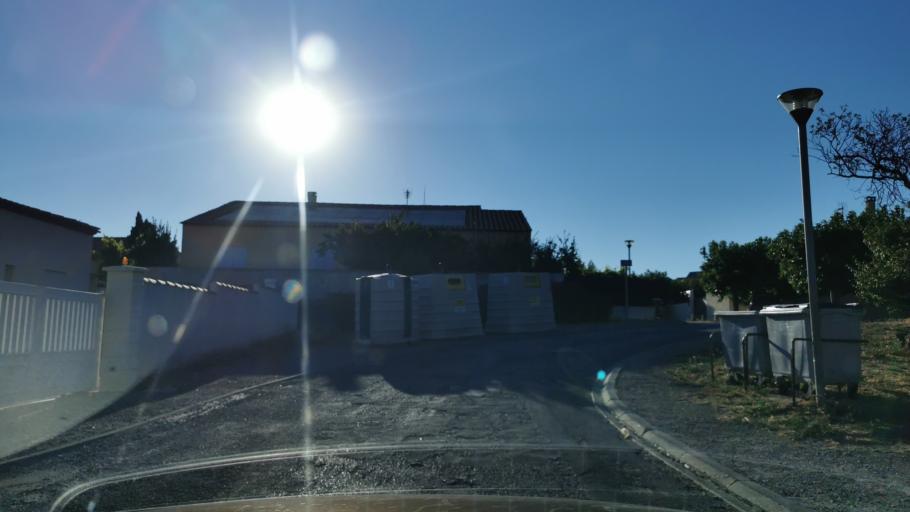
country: FR
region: Languedoc-Roussillon
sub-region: Departement de l'Aude
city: Ouveillan
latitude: 43.2872
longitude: 2.9639
